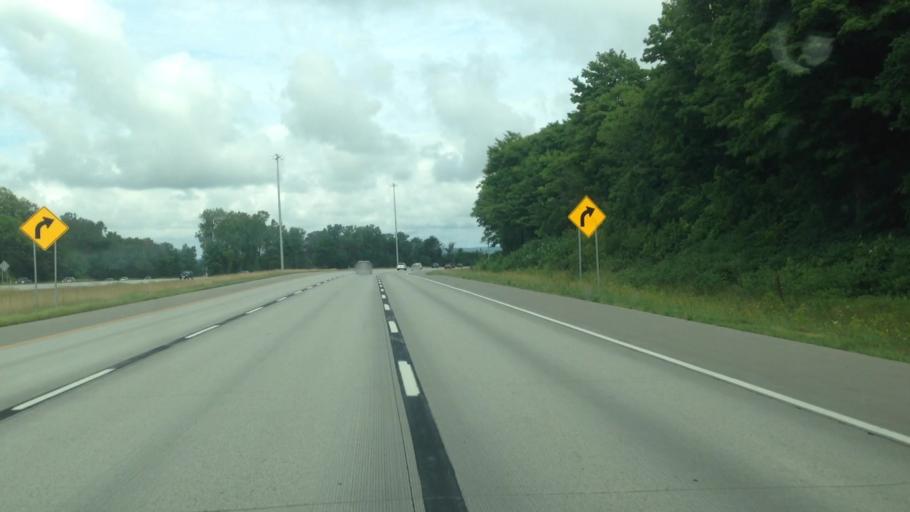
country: CA
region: Quebec
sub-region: Laurentides
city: Saint-Jerome
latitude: 45.7120
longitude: -73.9661
